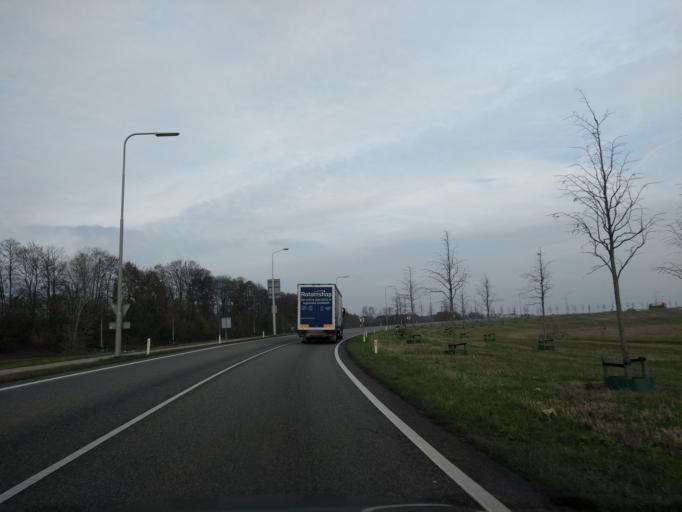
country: NL
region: Limburg
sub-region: Gemeente Sittard-Geleen
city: Born
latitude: 51.0711
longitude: 5.8200
